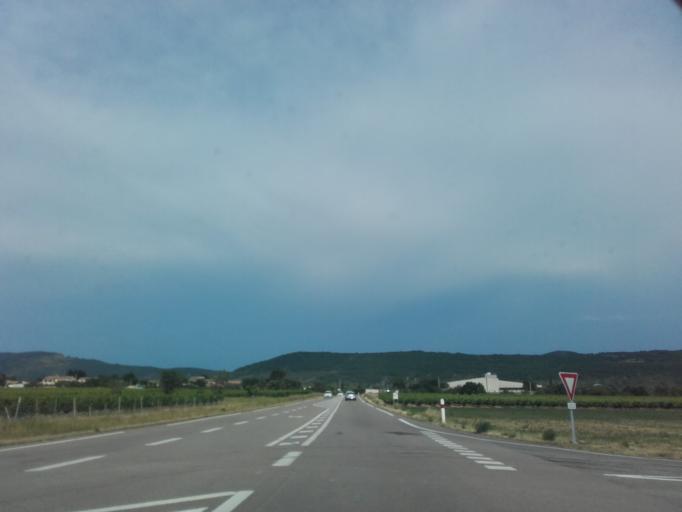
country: FR
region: Rhone-Alpes
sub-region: Departement de l'Ardeche
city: Alba-la-Romaine
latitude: 44.5675
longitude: 4.5963
